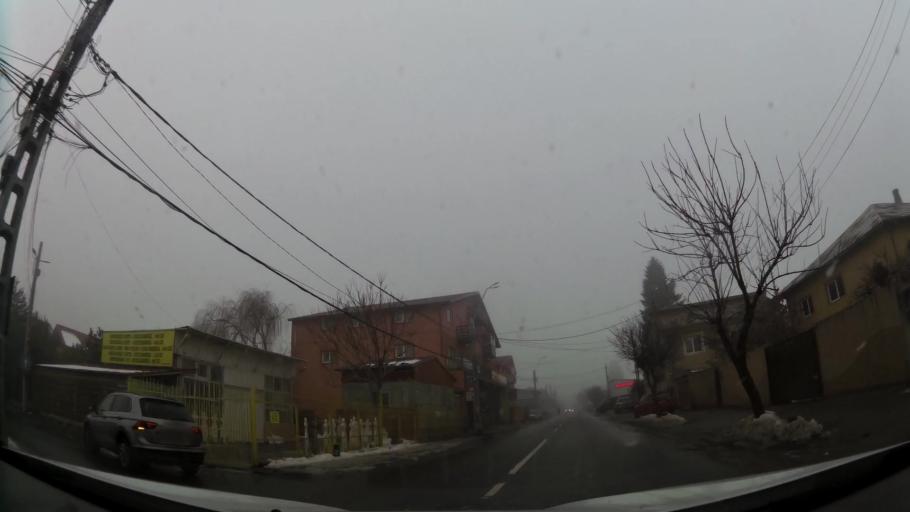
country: RO
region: Ilfov
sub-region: Comuna Chiajna
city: Chiajna
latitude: 44.4604
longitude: 25.9855
